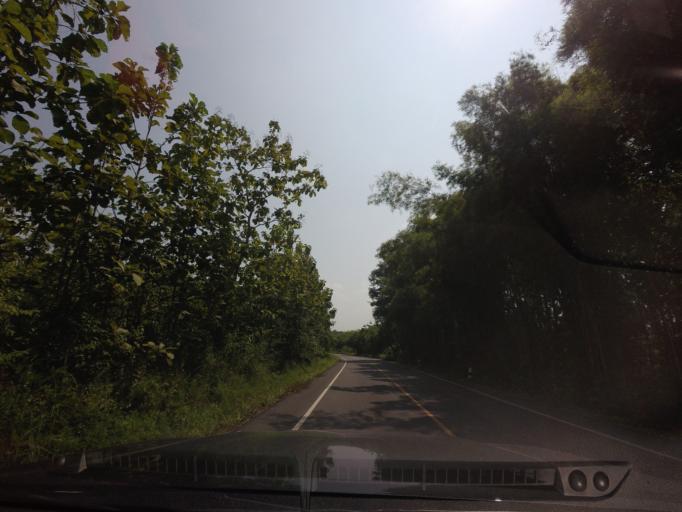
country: TH
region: Nan
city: Nan
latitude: 18.8547
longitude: 100.7924
